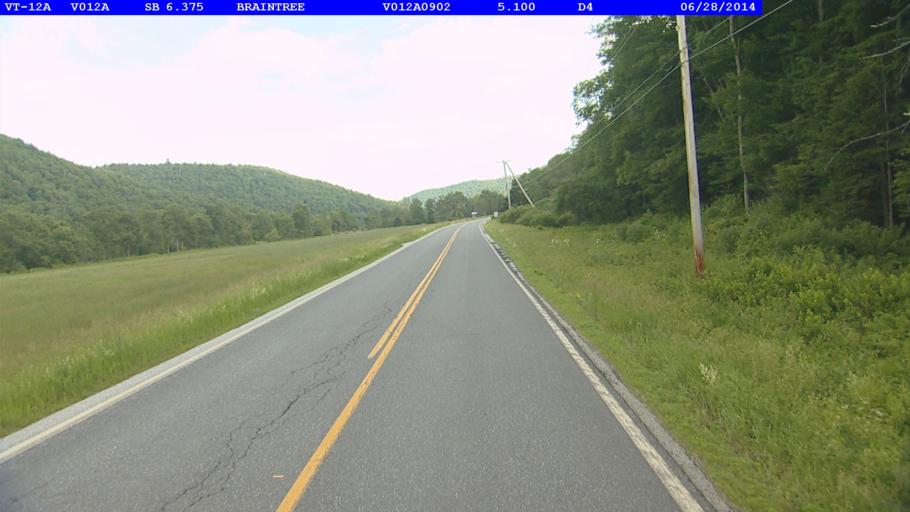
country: US
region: Vermont
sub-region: Orange County
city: Randolph
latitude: 43.9810
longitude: -72.7511
